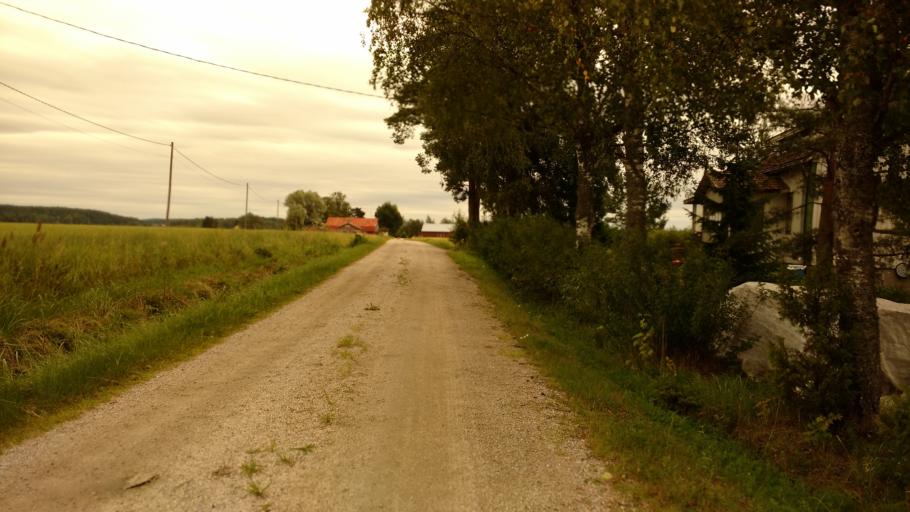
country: FI
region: Varsinais-Suomi
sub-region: Turku
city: Paimio
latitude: 60.4161
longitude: 22.8409
